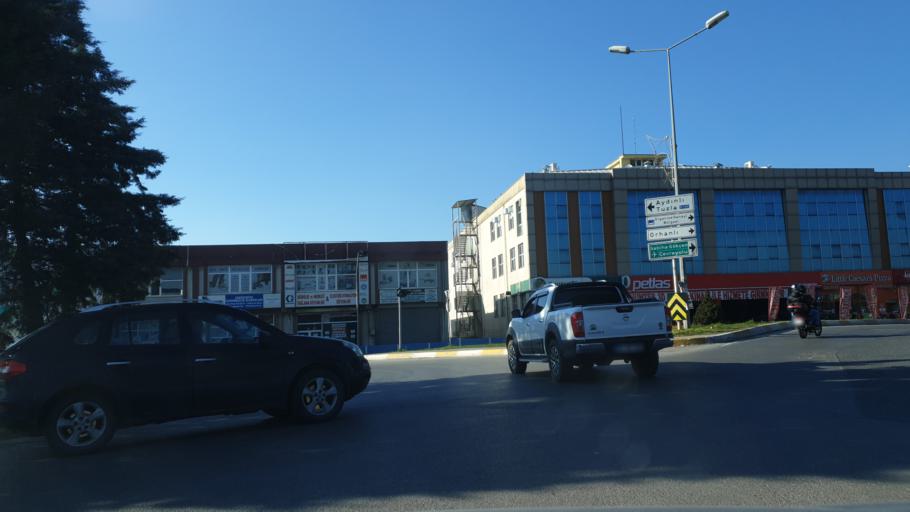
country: TR
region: Istanbul
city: Icmeler
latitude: 40.8817
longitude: 29.3472
